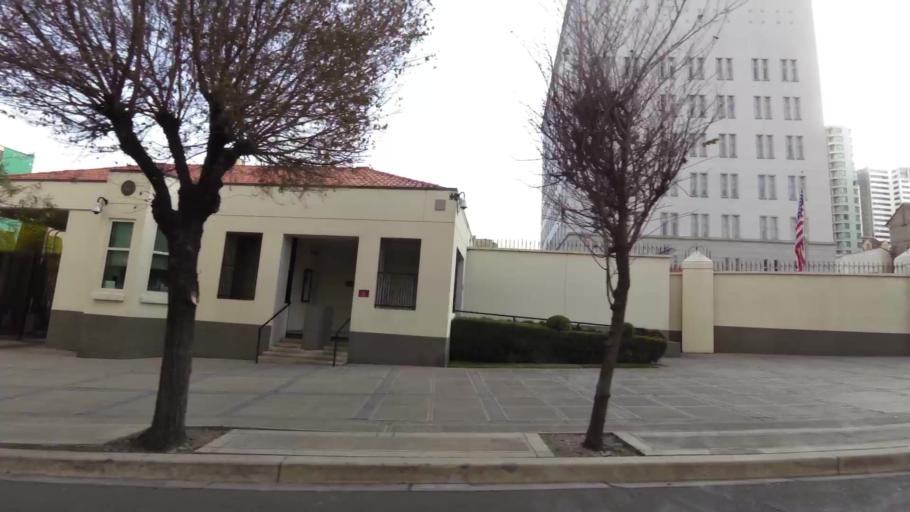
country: BO
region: La Paz
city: La Paz
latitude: -16.5127
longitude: -68.1213
